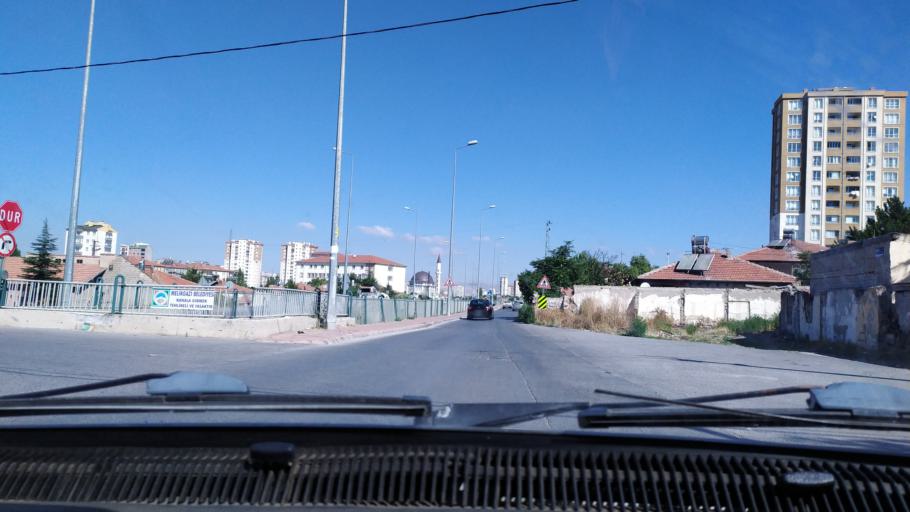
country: TR
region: Kayseri
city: Talas
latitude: 38.7279
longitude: 35.5502
